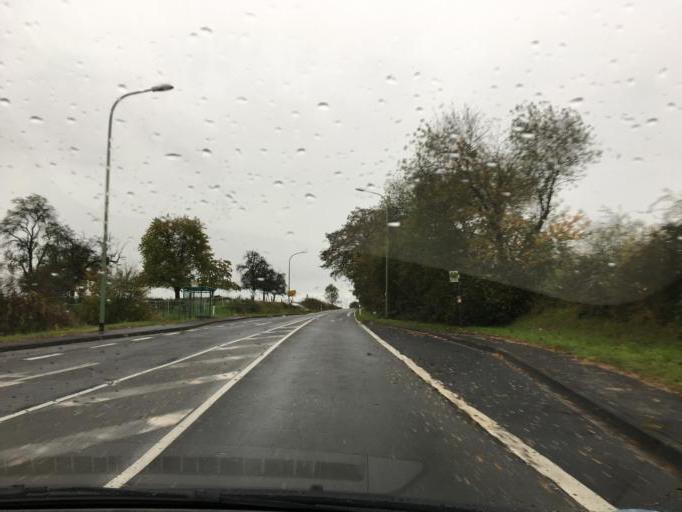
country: DE
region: North Rhine-Westphalia
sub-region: Regierungsbezirk Koln
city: Vettweiss
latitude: 50.7116
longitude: 6.5713
